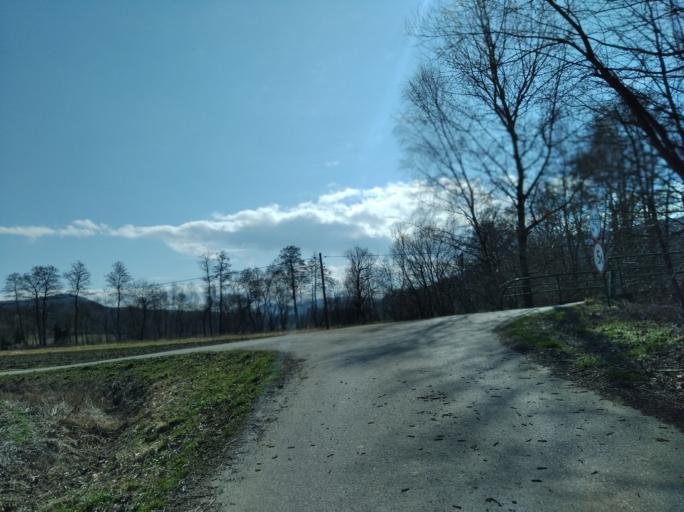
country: PL
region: Subcarpathian Voivodeship
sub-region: Powiat strzyzowski
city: Wysoka Strzyzowska
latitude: 49.8088
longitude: 21.7484
